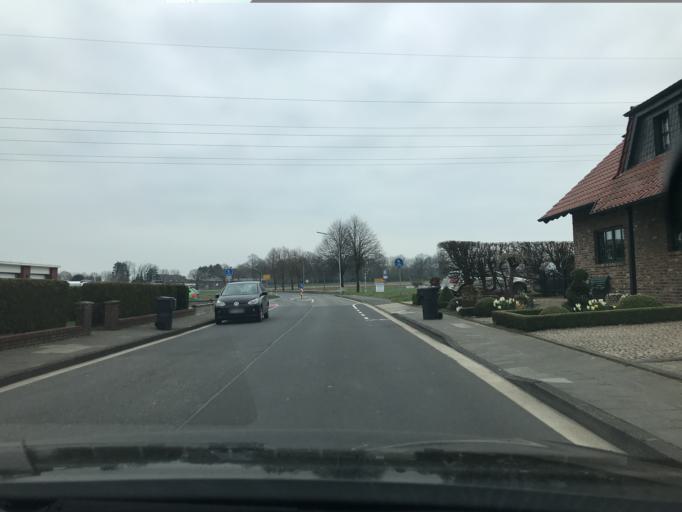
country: DE
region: North Rhine-Westphalia
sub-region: Regierungsbezirk Dusseldorf
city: Schwalmtal
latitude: 51.2201
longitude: 6.2459
